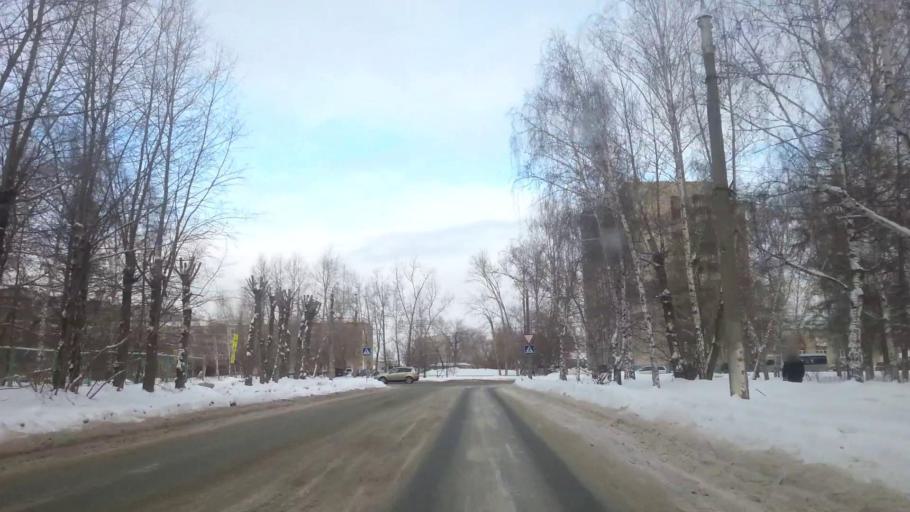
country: RU
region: Altai Krai
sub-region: Gorod Barnaulskiy
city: Barnaul
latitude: 53.3691
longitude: 83.6938
